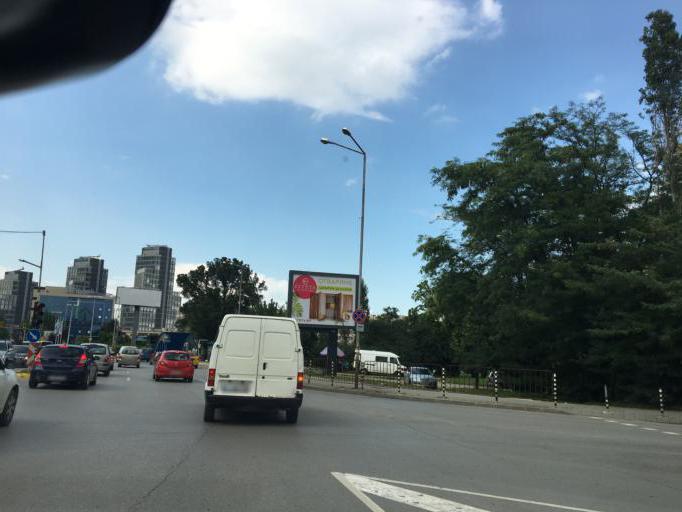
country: BG
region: Sofia-Capital
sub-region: Stolichna Obshtina
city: Sofia
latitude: 42.6618
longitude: 23.3589
